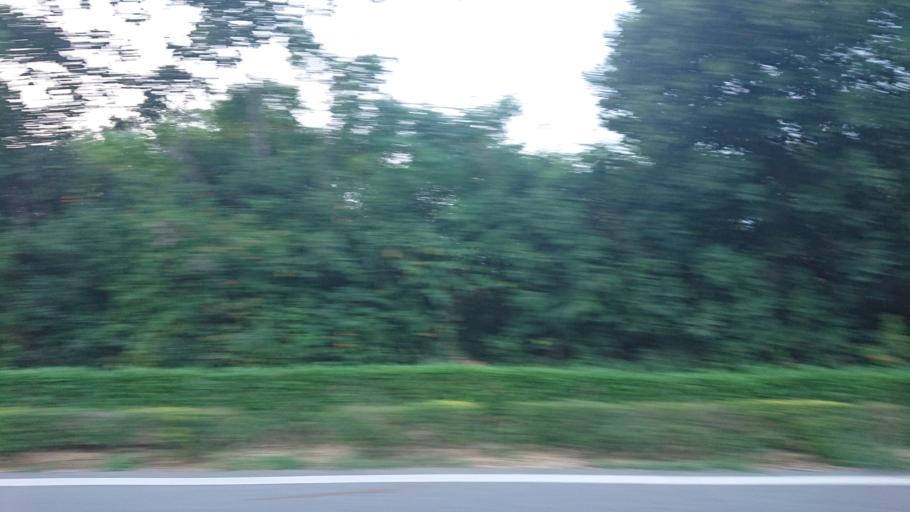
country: TW
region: Fukien
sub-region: Kinmen
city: Jincheng
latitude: 24.4590
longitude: 118.3229
